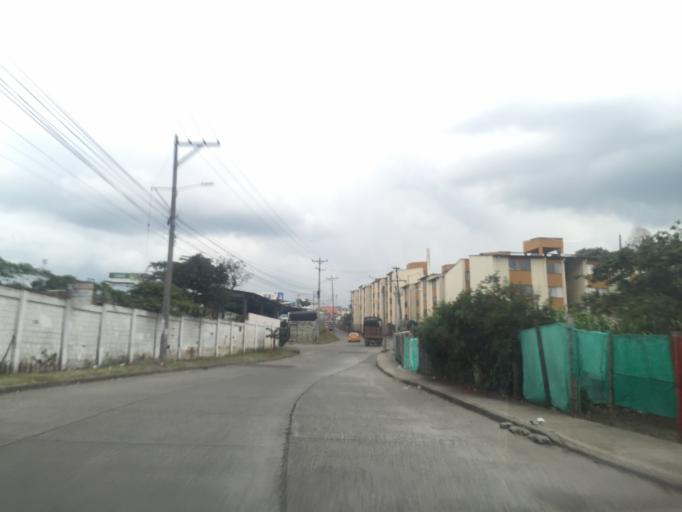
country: CO
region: Quindio
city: Armenia
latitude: 4.5305
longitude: -75.6790
